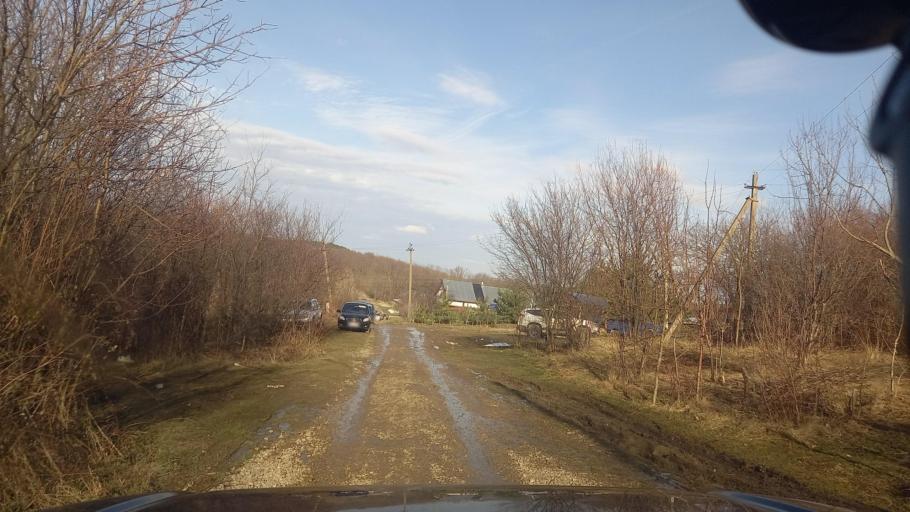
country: RU
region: Krasnodarskiy
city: Goryachiy Klyuch
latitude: 44.6872
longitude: 38.9803
